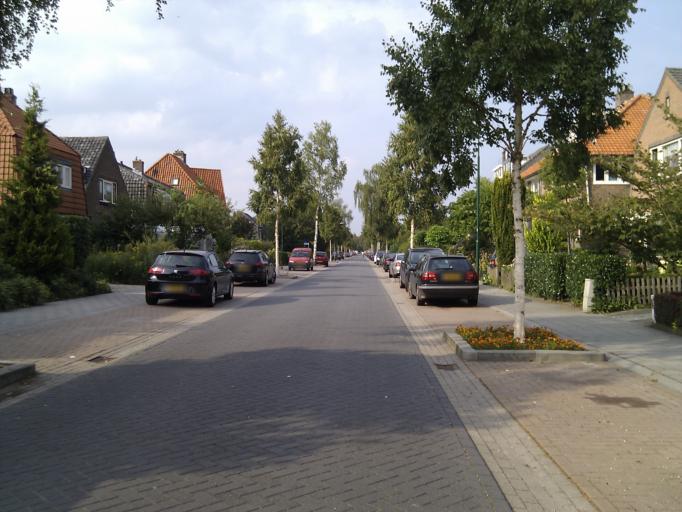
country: NL
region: Utrecht
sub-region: Gemeente De Bilt
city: De Bilt
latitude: 52.1107
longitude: 5.1779
